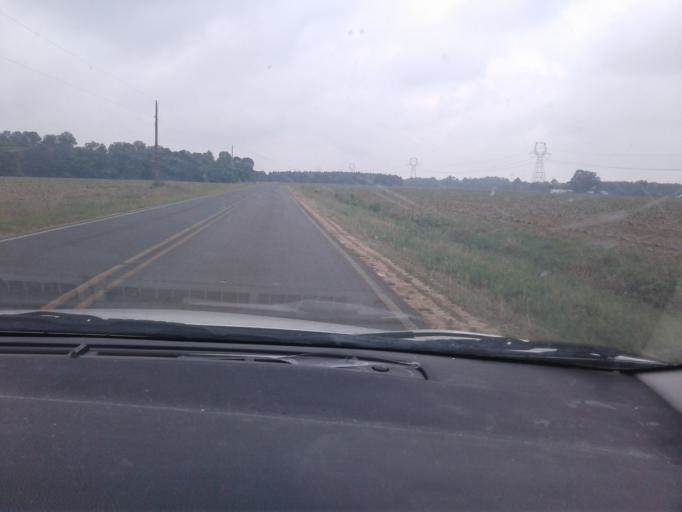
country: US
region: North Carolina
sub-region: Harnett County
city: Coats
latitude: 35.3708
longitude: -78.6483
